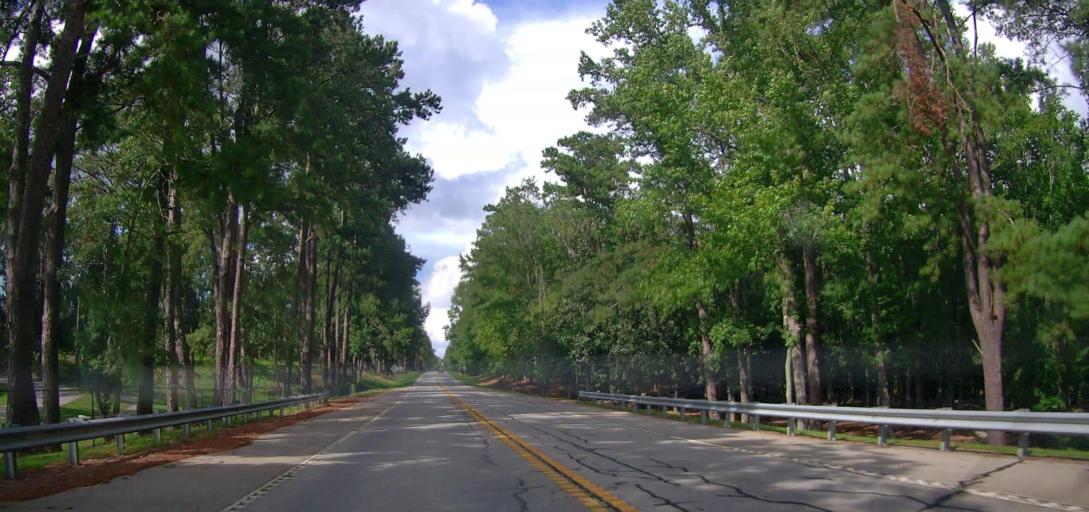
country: US
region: Georgia
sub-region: Harris County
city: Pine Mountain
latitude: 32.8328
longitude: -84.8437
